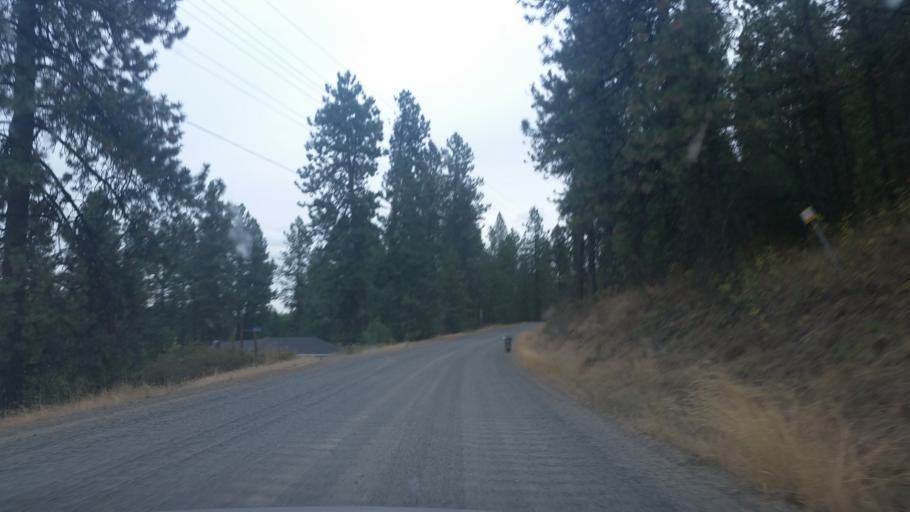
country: US
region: Washington
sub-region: Spokane County
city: Cheney
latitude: 47.5371
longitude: -117.5869
